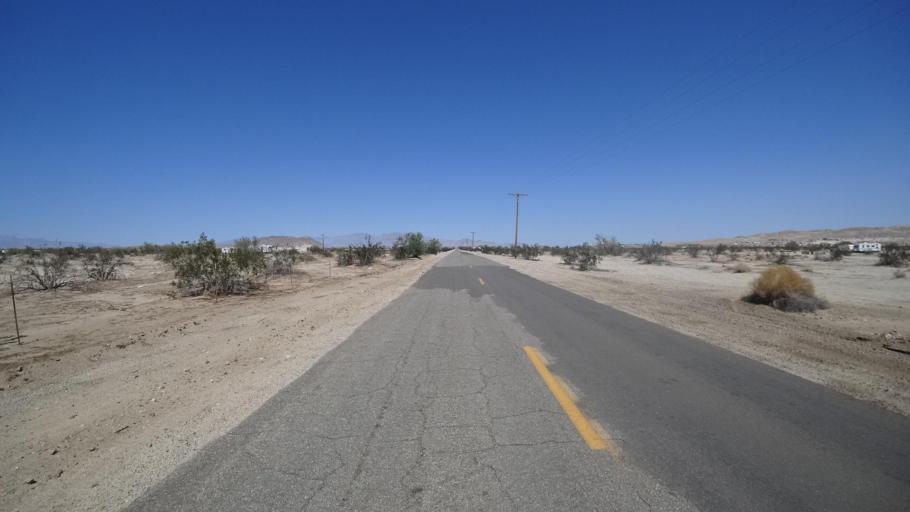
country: US
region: California
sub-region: Imperial County
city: Salton City
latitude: 33.1132
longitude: -116.1328
